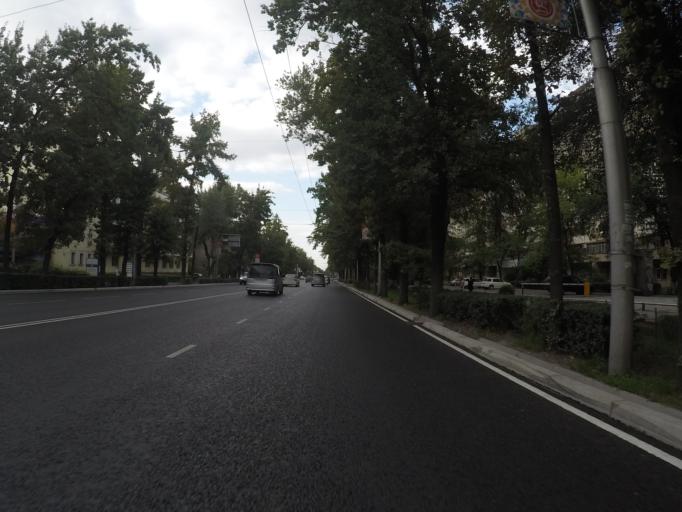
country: KG
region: Chuy
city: Bishkek
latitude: 42.8708
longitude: 74.5878
